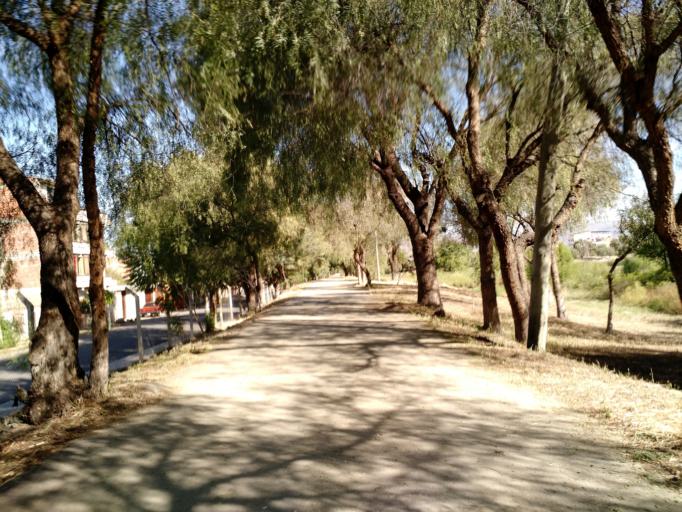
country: BO
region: Cochabamba
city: Cochabamba
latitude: -17.3867
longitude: -66.2046
